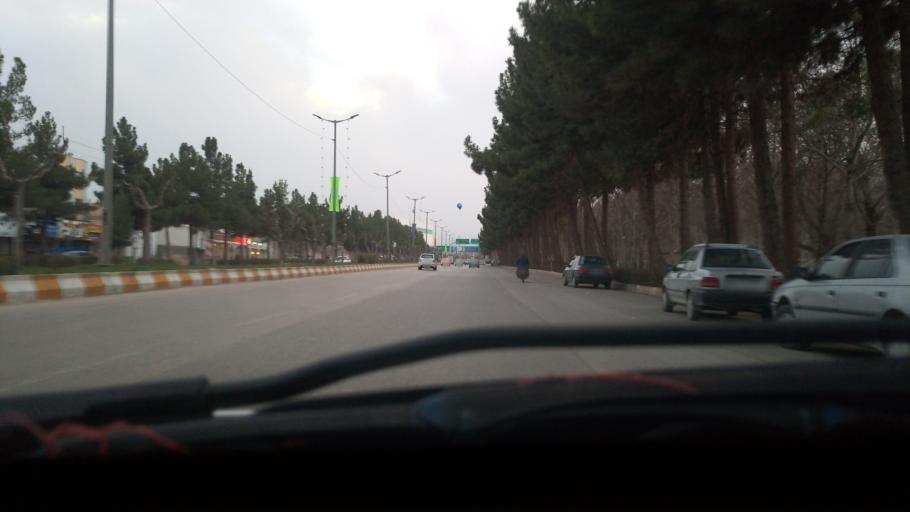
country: IR
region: Khorasan-e Shomali
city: Bojnurd
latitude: 37.4721
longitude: 57.3515
